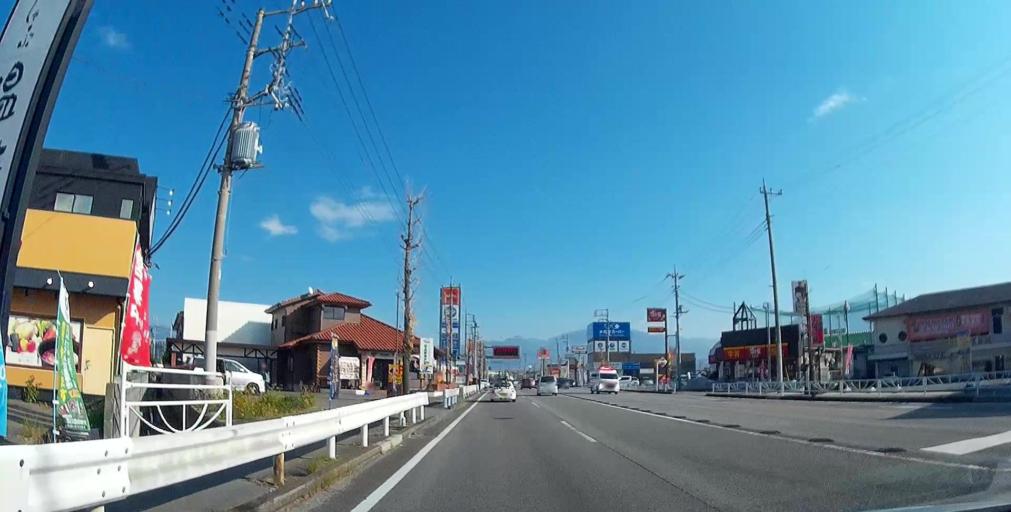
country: JP
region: Yamanashi
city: Isawa
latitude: 35.6438
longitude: 138.6256
